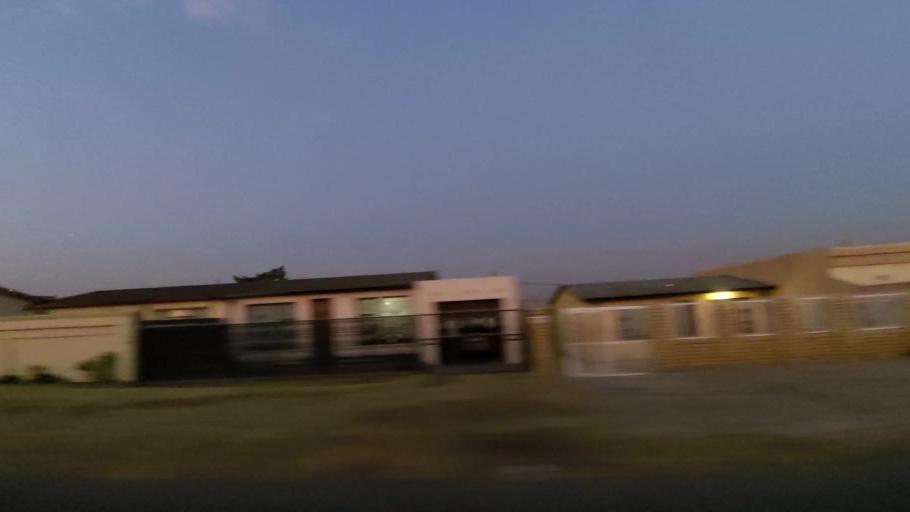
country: ZA
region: Gauteng
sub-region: City of Johannesburg Metropolitan Municipality
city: Roodepoort
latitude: -26.2198
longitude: 27.9089
